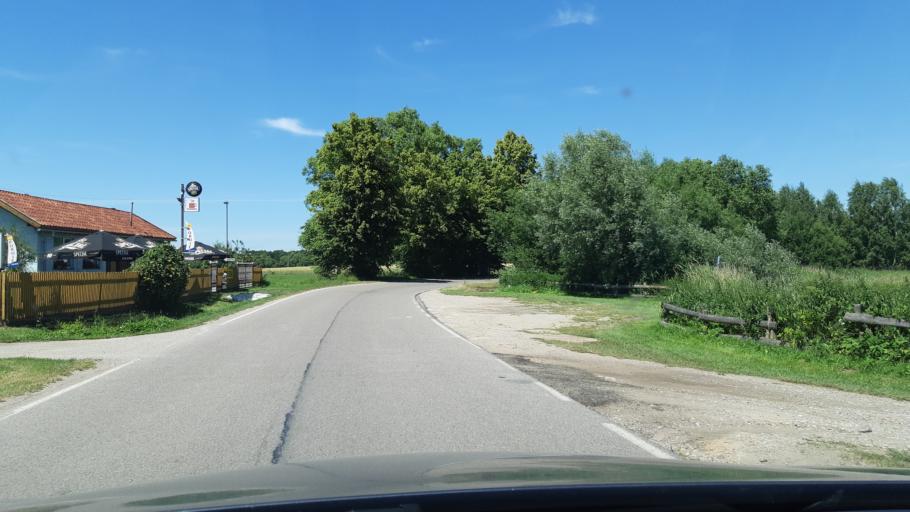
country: PL
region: Warmian-Masurian Voivodeship
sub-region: Powiat gizycki
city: Ryn
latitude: 53.8978
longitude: 21.6615
